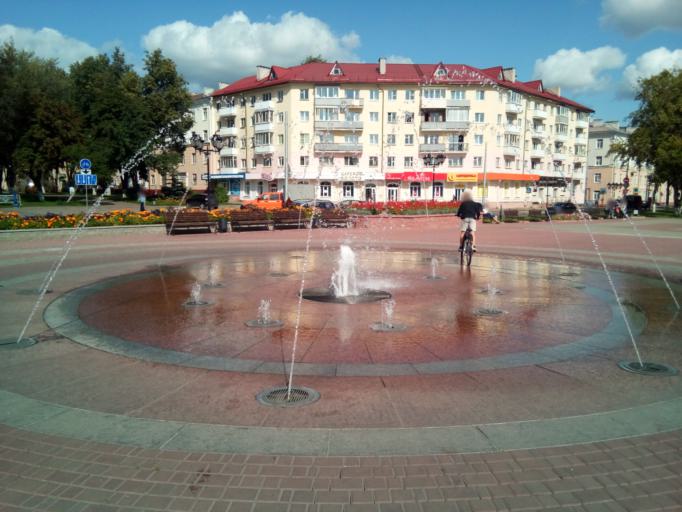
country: BY
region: Vitebsk
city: Polatsk
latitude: 55.4846
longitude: 28.7776
